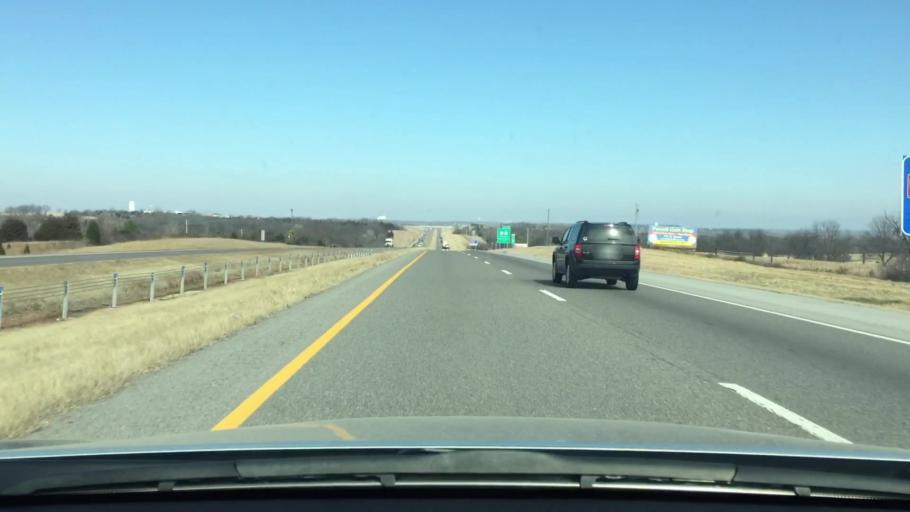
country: US
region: Oklahoma
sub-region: McClain County
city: Purcell
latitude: 34.9633
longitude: -97.3696
